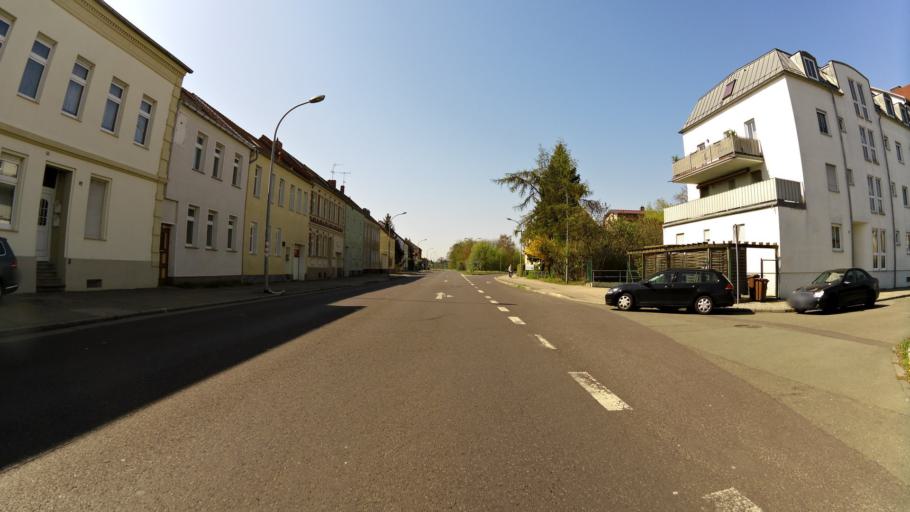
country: DE
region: Saxony-Anhalt
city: Stendal
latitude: 52.5926
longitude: 11.8507
